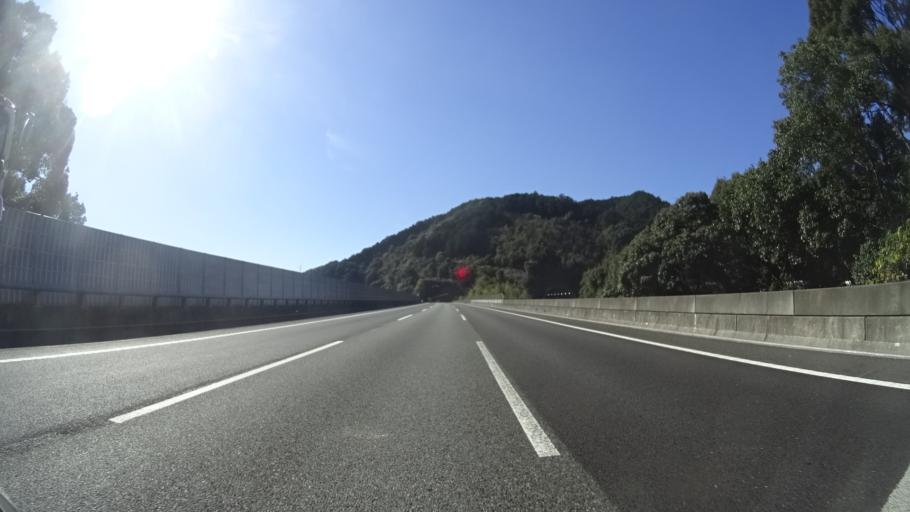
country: JP
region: Shizuoka
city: Shizuoka-shi
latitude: 35.0093
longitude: 138.3171
